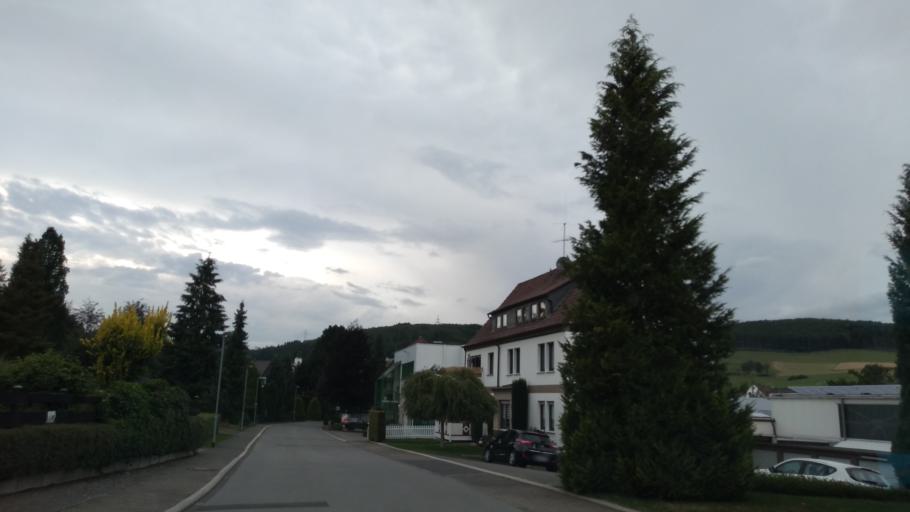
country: DE
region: North Rhine-Westphalia
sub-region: Regierungsbezirk Arnsberg
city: Herscheid
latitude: 51.1890
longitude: 7.8036
